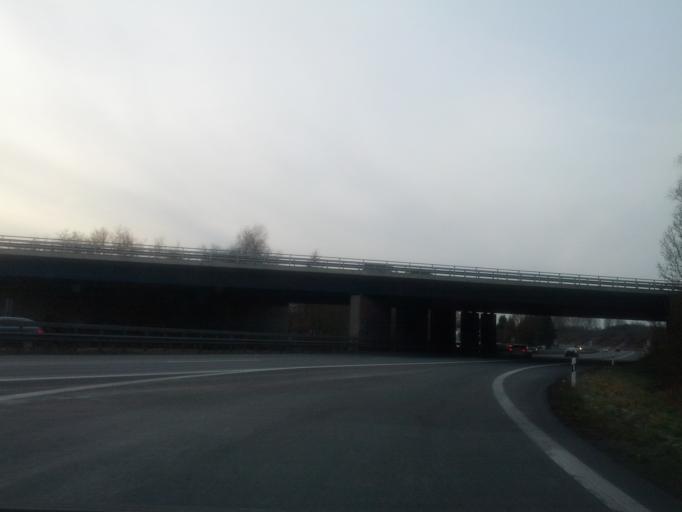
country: DE
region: Lower Saxony
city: Harmstorf
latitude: 53.3810
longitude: 10.0072
